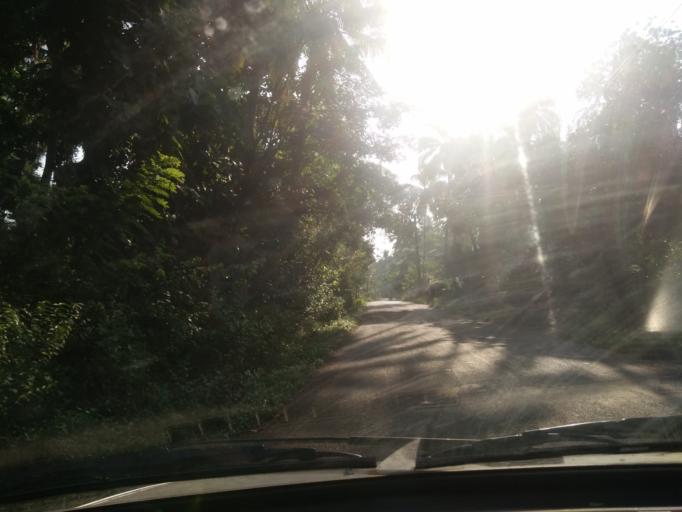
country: IN
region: Goa
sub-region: South Goa
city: Cuncolim
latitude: 15.1801
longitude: 73.9738
